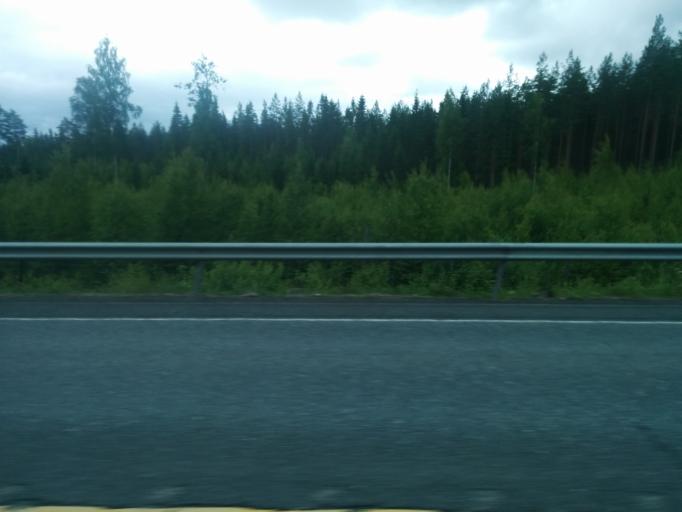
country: FI
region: Pirkanmaa
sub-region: Tampere
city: Orivesi
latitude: 61.6785
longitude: 24.3219
